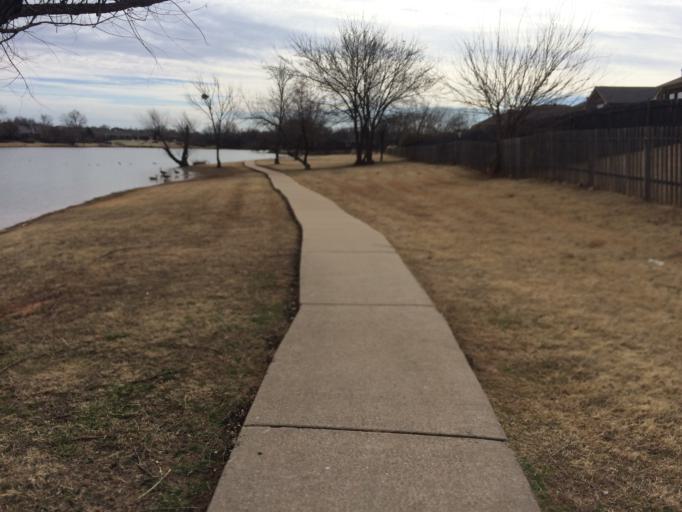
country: US
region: Oklahoma
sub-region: Cleveland County
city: Hall Park
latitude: 35.2251
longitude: -97.4026
